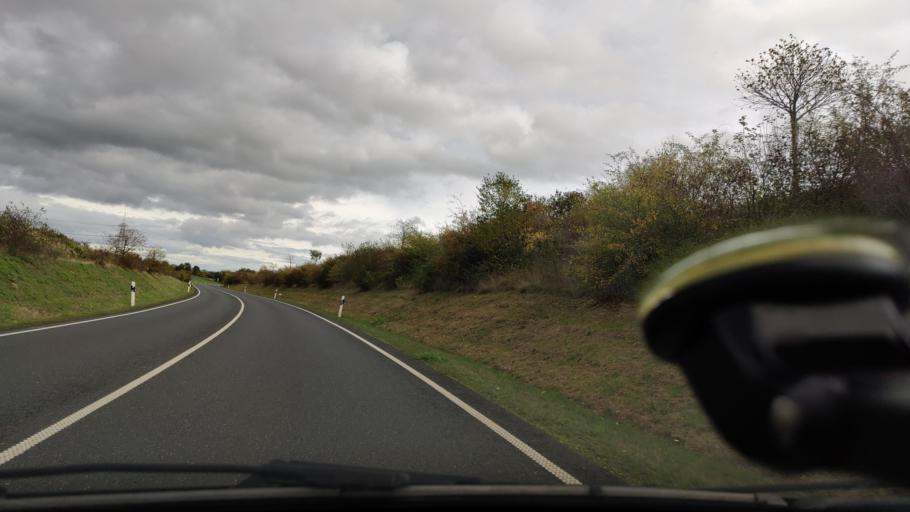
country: DE
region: North Rhine-Westphalia
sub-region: Regierungsbezirk Koln
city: Heinsberg
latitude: 51.0466
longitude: 6.0920
